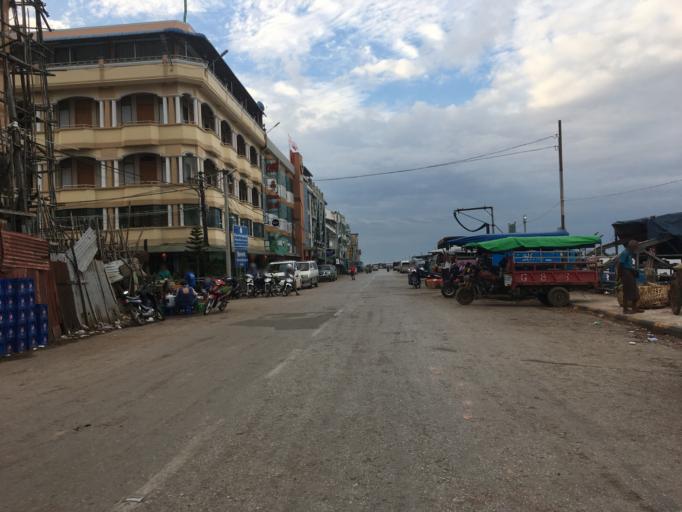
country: MM
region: Mon
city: Mawlamyine
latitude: 16.4953
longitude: 97.6178
